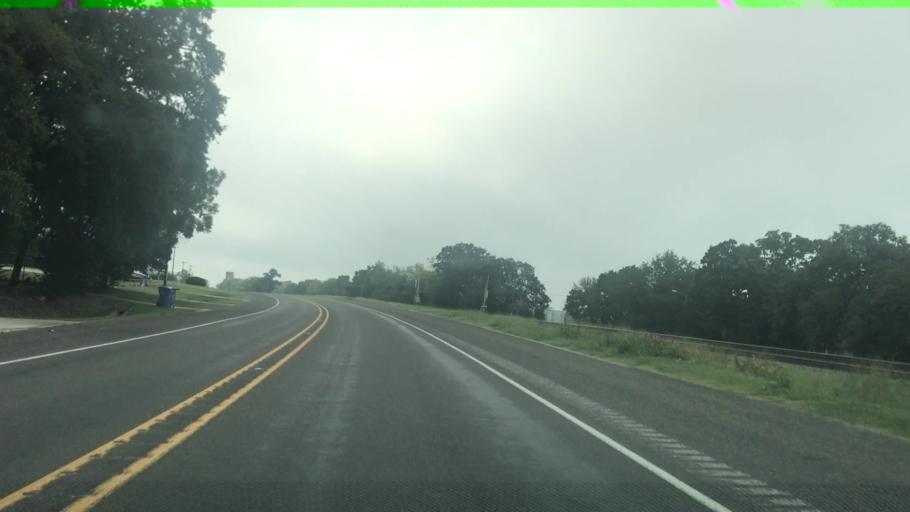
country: US
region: Texas
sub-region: Houston County
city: Cooper
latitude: 31.1215
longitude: -95.4448
